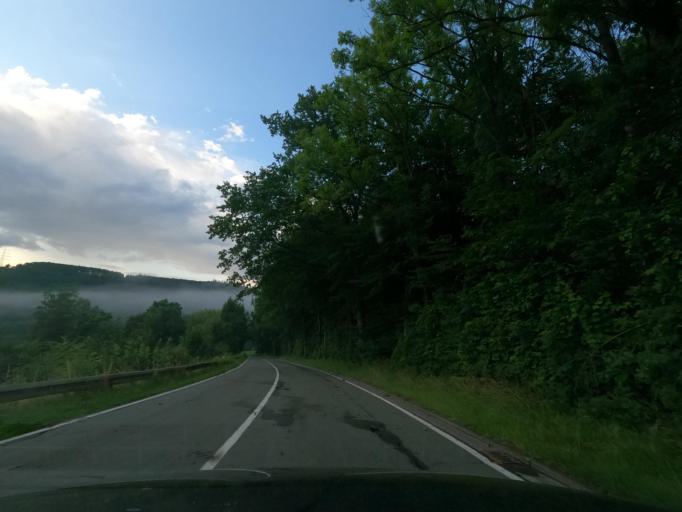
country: DE
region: North Rhine-Westphalia
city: Plettenberg
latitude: 51.2347
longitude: 7.9012
